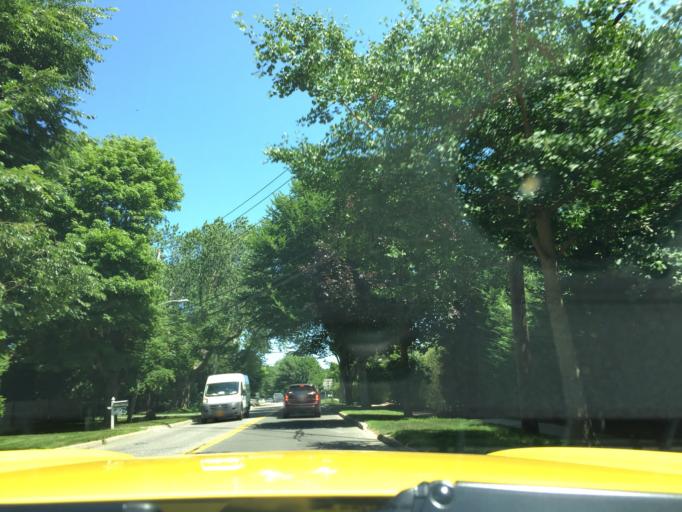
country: US
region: New York
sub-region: Suffolk County
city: East Hampton
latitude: 40.9584
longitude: -72.2022
